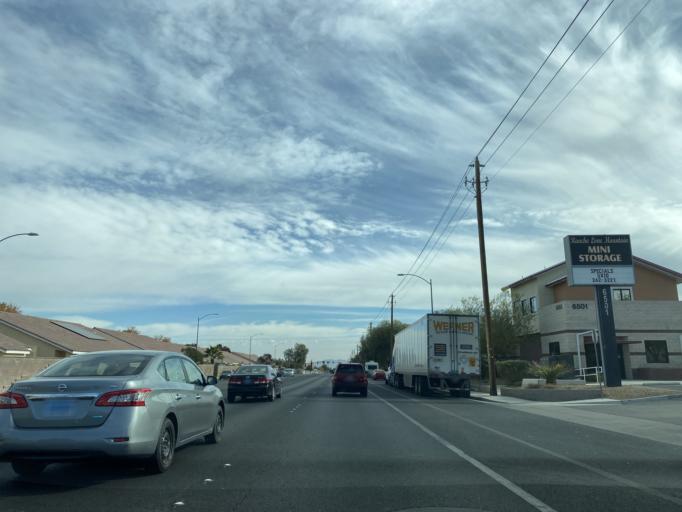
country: US
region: Nevada
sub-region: Clark County
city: Las Vegas
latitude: 36.2474
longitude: -115.2378
